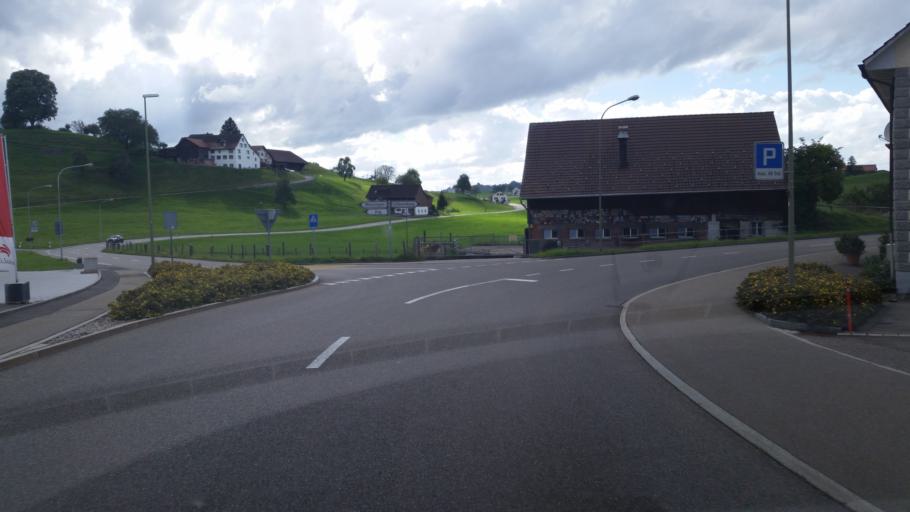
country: CH
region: Zurich
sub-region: Bezirk Horgen
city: Waedenswil / Eichweid
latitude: 47.1753
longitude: 8.6621
